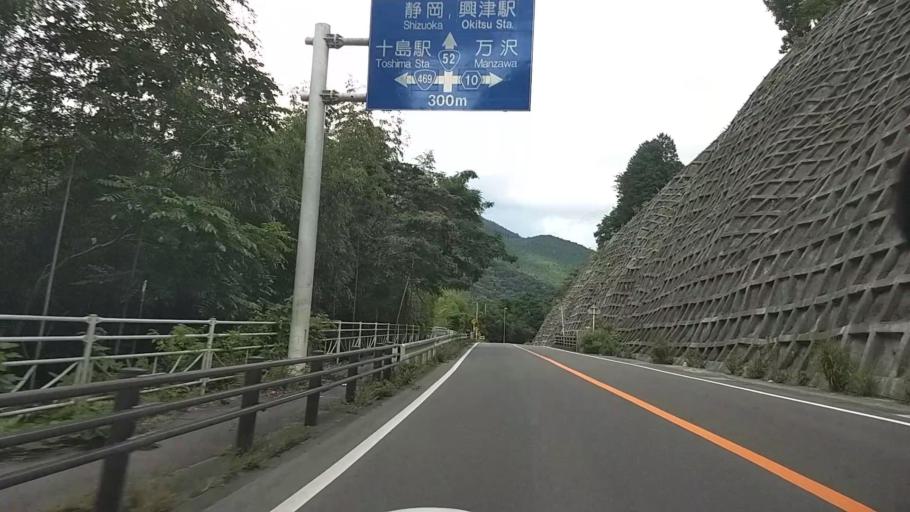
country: JP
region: Shizuoka
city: Fujinomiya
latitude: 35.2257
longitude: 138.5144
